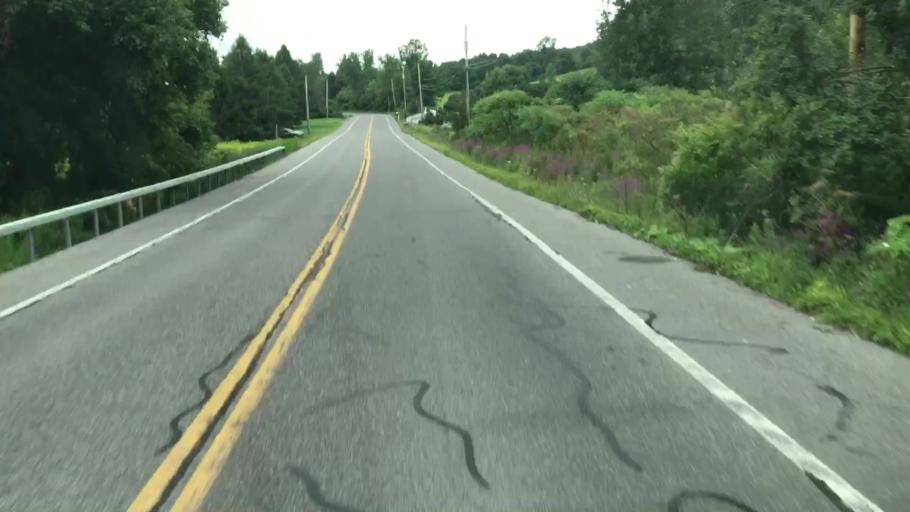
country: US
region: New York
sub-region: Onondaga County
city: Camillus
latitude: 43.0652
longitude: -76.3233
